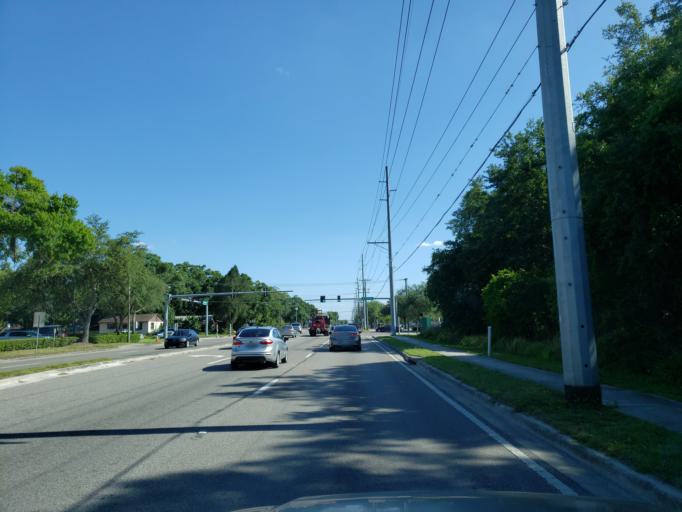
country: US
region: Florida
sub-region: Hillsborough County
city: Mango
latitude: 27.9676
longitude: -82.3352
